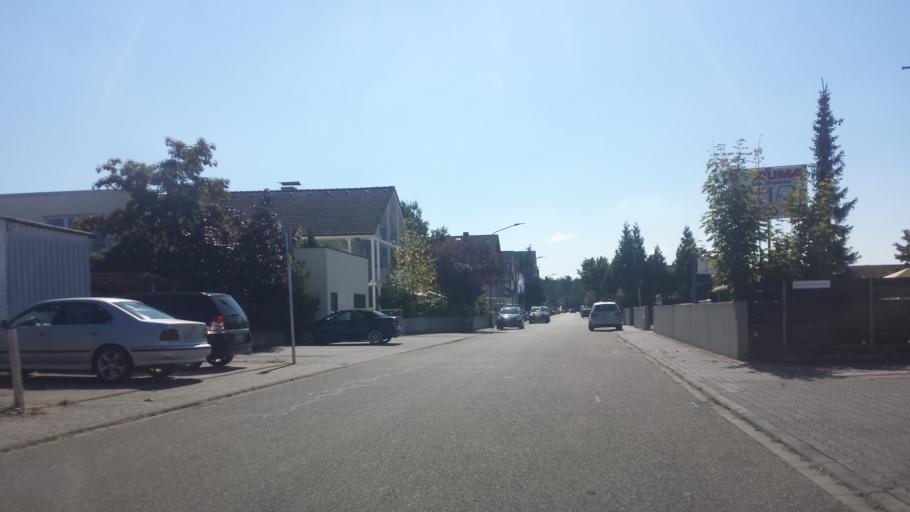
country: DE
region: Hesse
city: Lorsch
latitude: 49.6393
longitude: 8.5665
